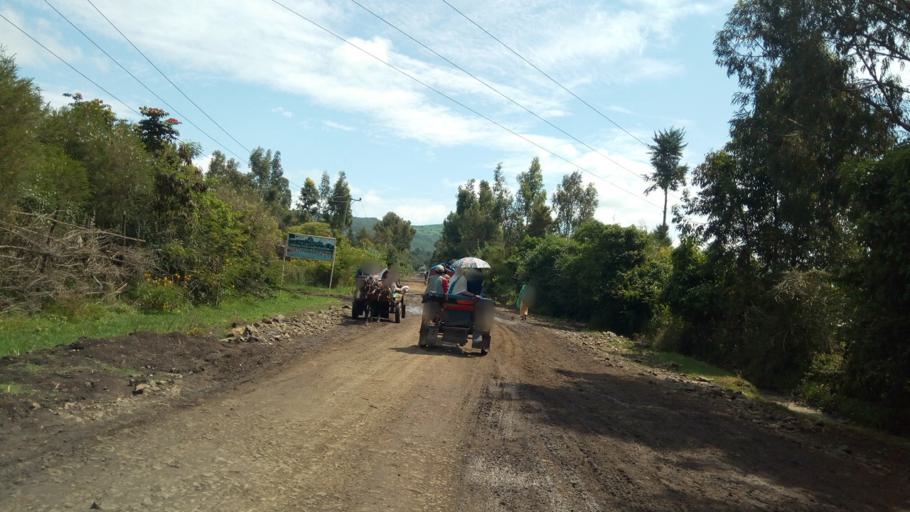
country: ET
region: Oromiya
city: Bishoftu
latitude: 8.8479
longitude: 39.0182
